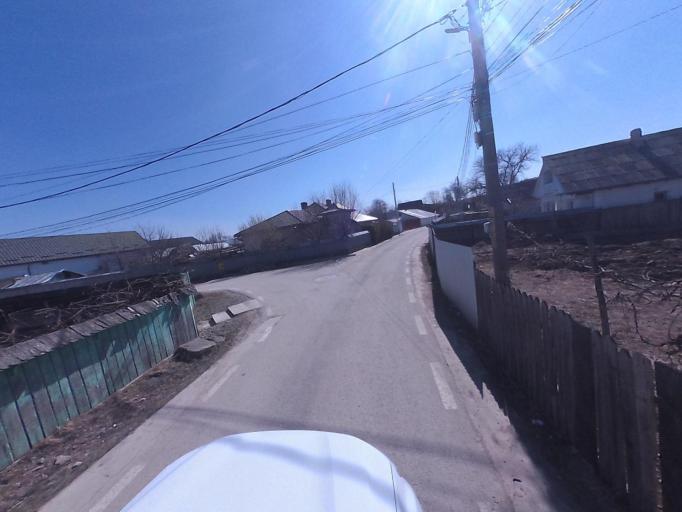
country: RO
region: Neamt
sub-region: Oras Targu Neamt
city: Humulesti
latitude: 47.1962
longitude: 26.3550
